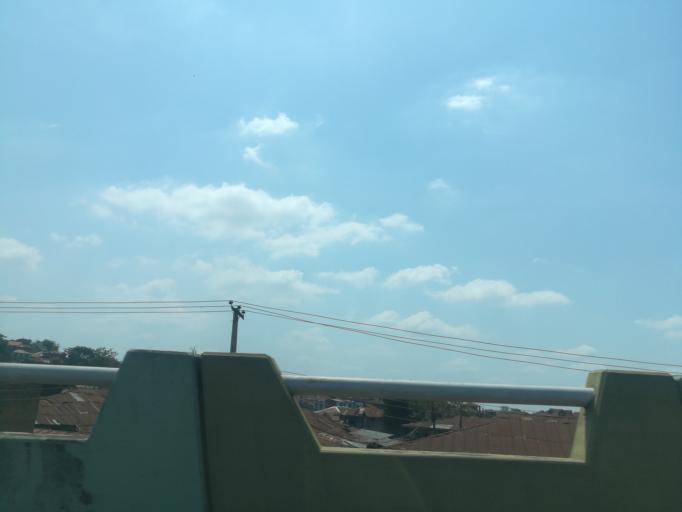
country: NG
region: Ogun
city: Abeokuta
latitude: 7.1567
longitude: 3.3425
